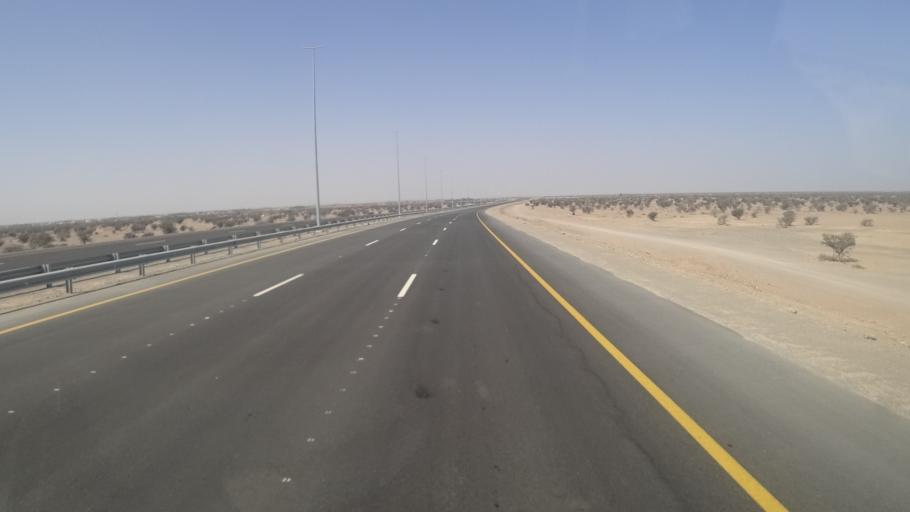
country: OM
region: Ash Sharqiyah
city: Sur
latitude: 22.2720
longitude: 59.2463
